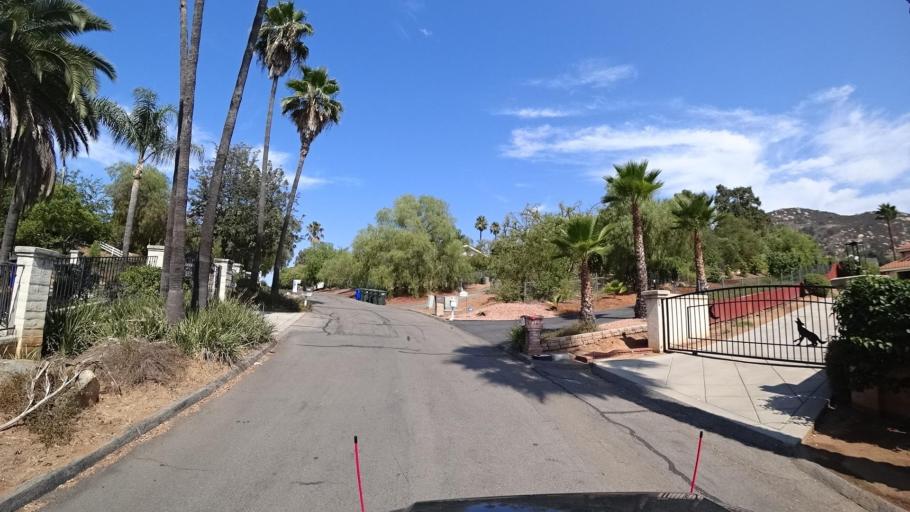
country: US
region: California
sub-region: San Diego County
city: Hidden Meadows
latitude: 33.1825
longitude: -117.1079
